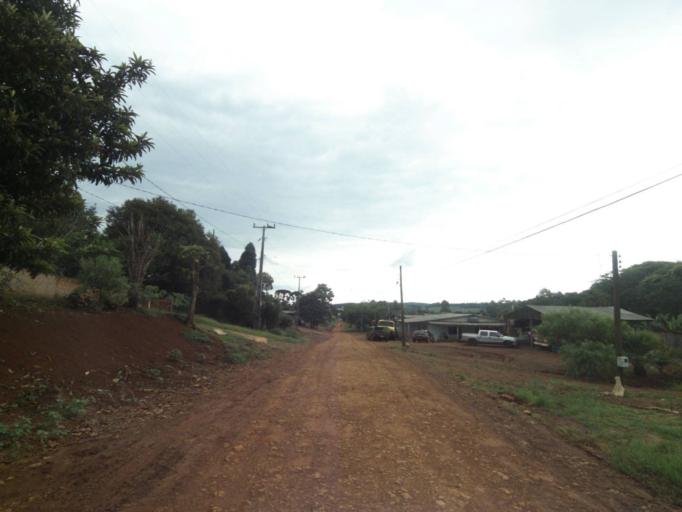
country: BR
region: Parana
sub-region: Pitanga
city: Pitanga
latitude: -24.8960
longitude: -51.9606
